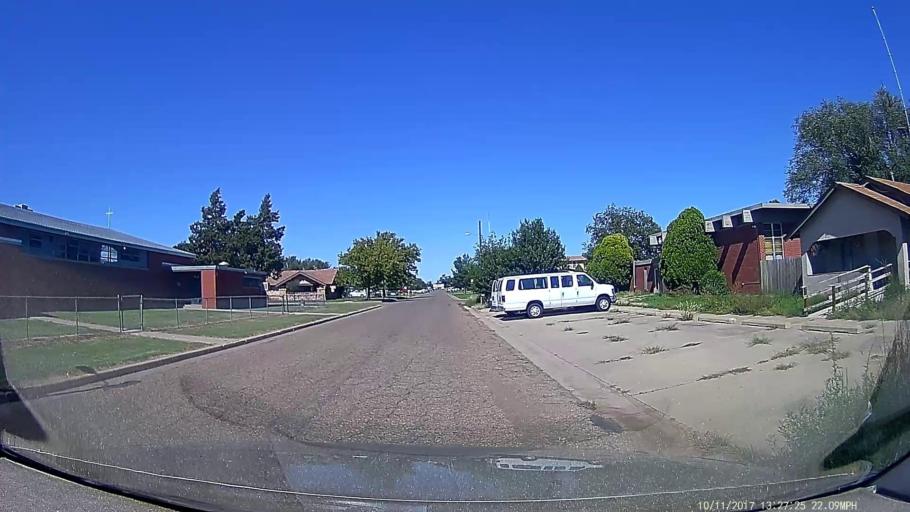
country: US
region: New Mexico
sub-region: Curry County
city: Clovis
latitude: 34.4086
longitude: -103.2092
